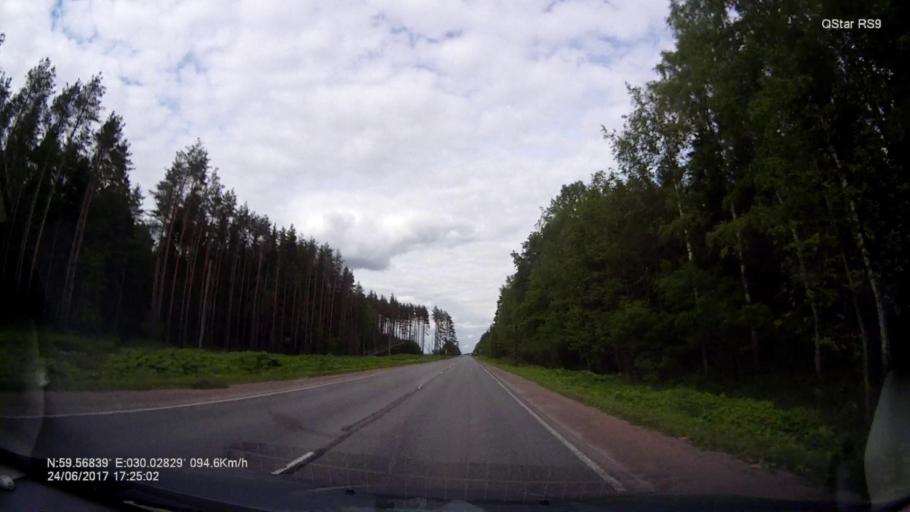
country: RU
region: Leningrad
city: Mariyenburg
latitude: 59.5685
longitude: 30.0287
